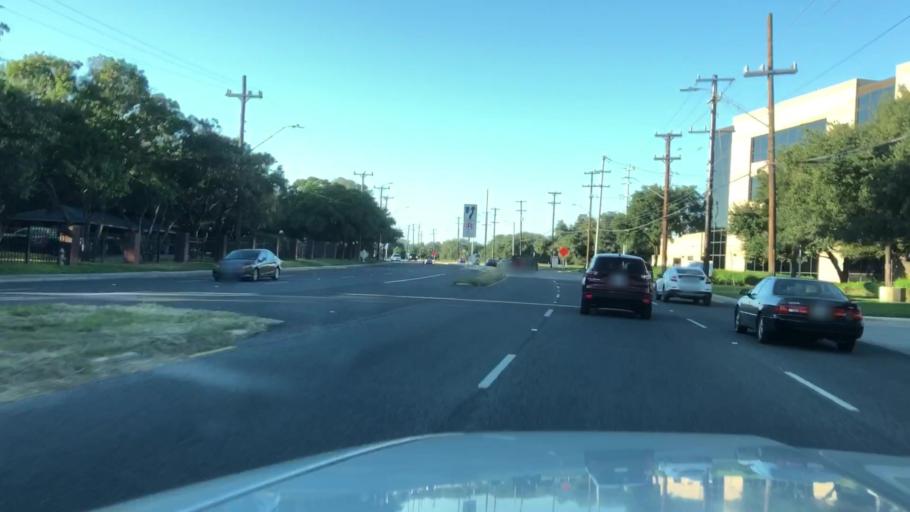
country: US
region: Texas
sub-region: Bexar County
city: Leon Valley
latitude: 29.5128
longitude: -98.5916
